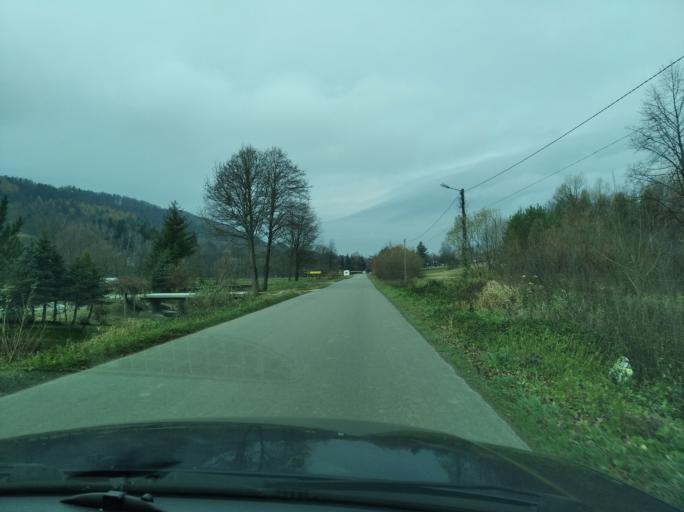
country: PL
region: Subcarpathian Voivodeship
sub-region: Powiat krosnienski
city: Odrzykon
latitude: 49.7809
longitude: 21.7638
